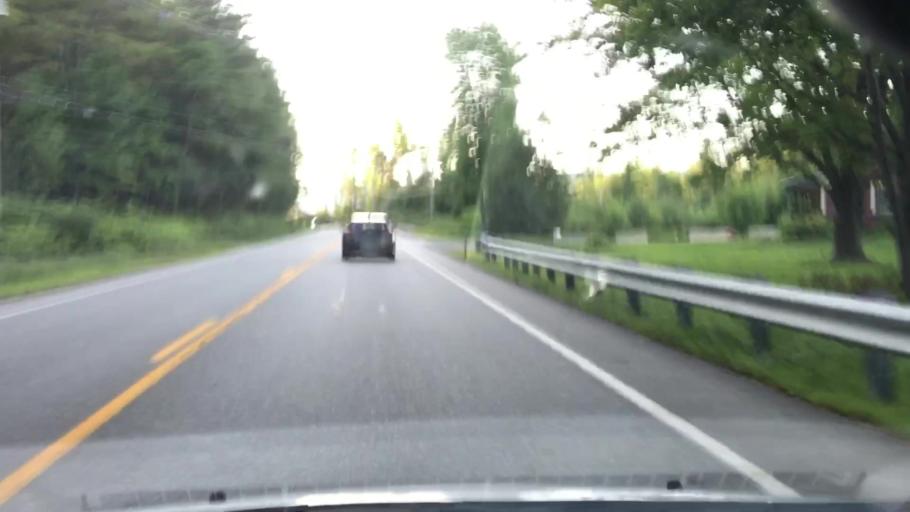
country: US
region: New Hampshire
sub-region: Grafton County
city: Rumney
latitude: 43.7789
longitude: -71.7736
